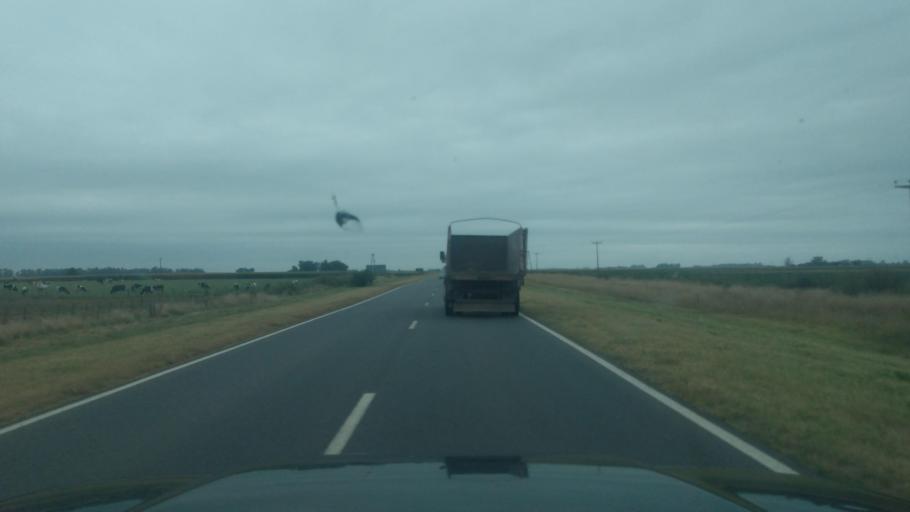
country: AR
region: Buenos Aires
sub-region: Partido de Nueve de Julio
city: Nueve de Julio
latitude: -35.3883
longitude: -60.7350
